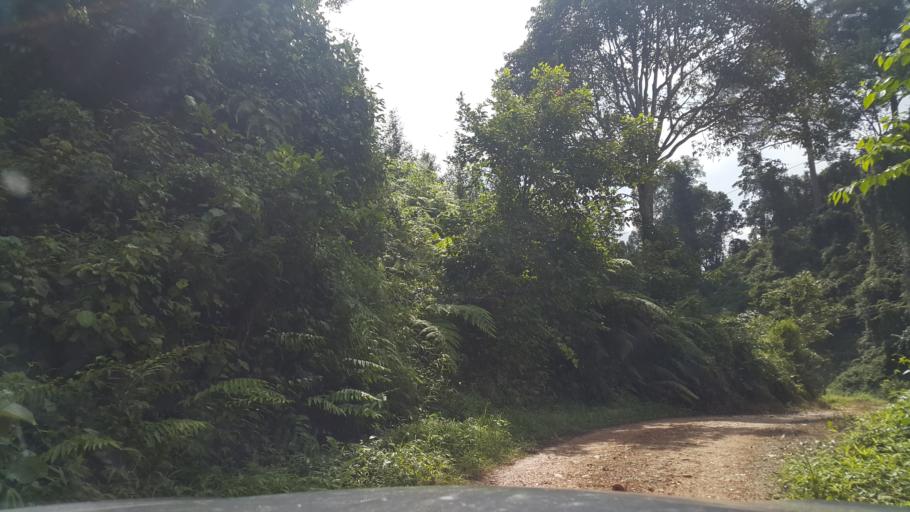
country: TH
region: Chiang Mai
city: Phrao
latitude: 19.1071
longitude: 99.2810
